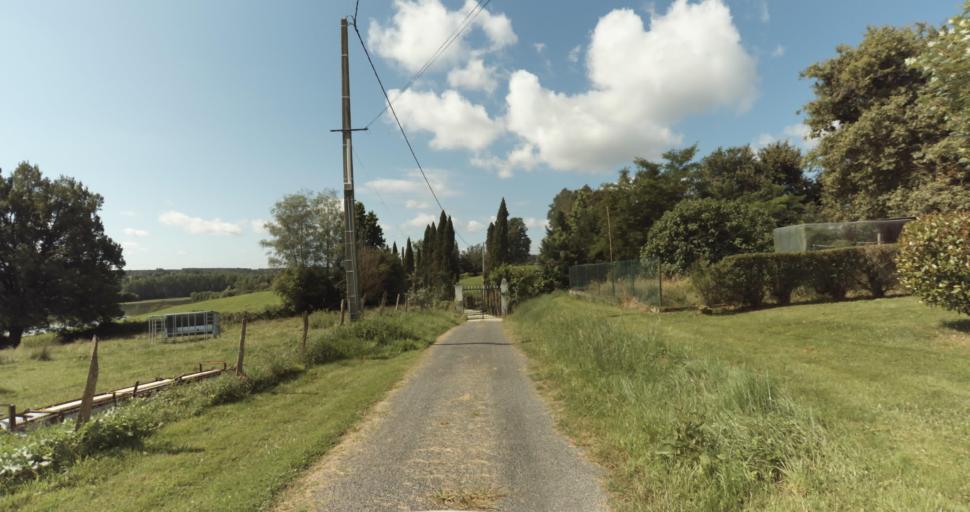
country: FR
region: Aquitaine
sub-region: Departement de la Gironde
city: Bazas
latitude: 44.4391
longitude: -0.1766
